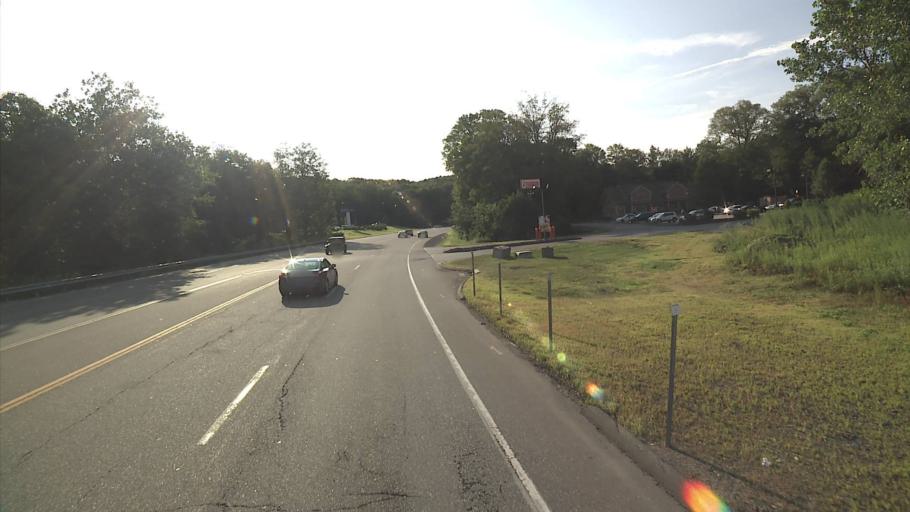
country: US
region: Connecticut
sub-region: New London County
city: Preston City
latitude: 41.4880
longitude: -71.9745
